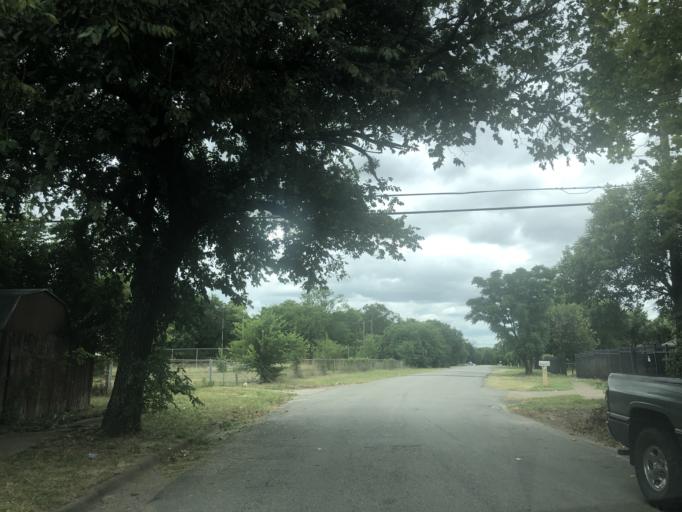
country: US
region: Texas
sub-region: Dallas County
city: Duncanville
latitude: 32.6403
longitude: -96.9059
